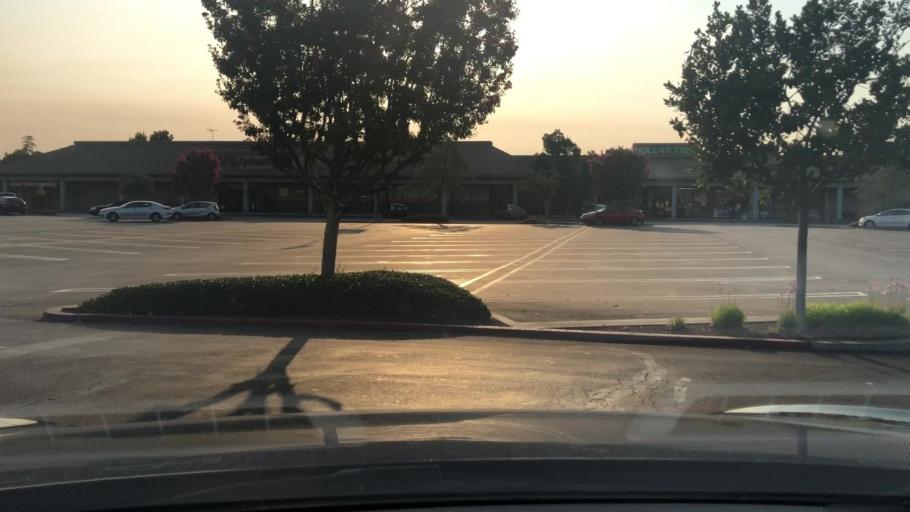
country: US
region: California
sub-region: Fresno County
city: Clovis
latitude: 36.8362
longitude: -119.7535
